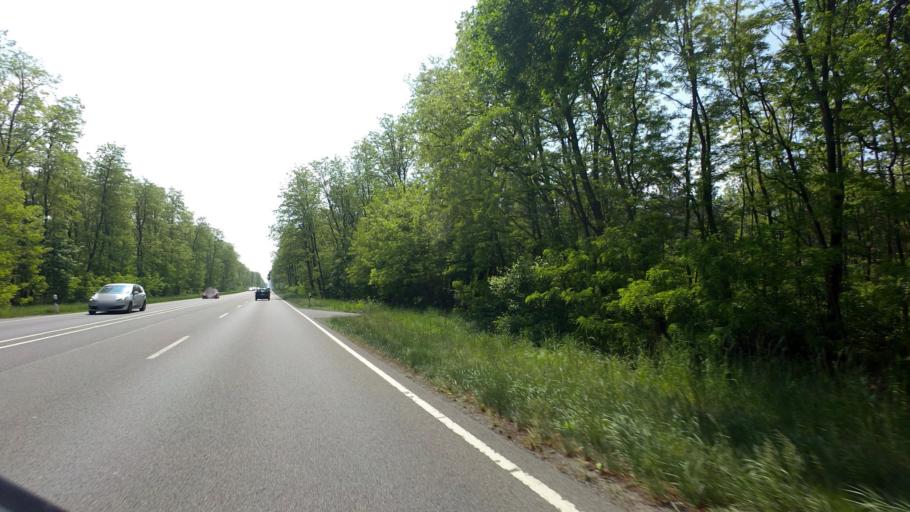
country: DE
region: Brandenburg
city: Spremberg
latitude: 51.6450
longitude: 14.3615
